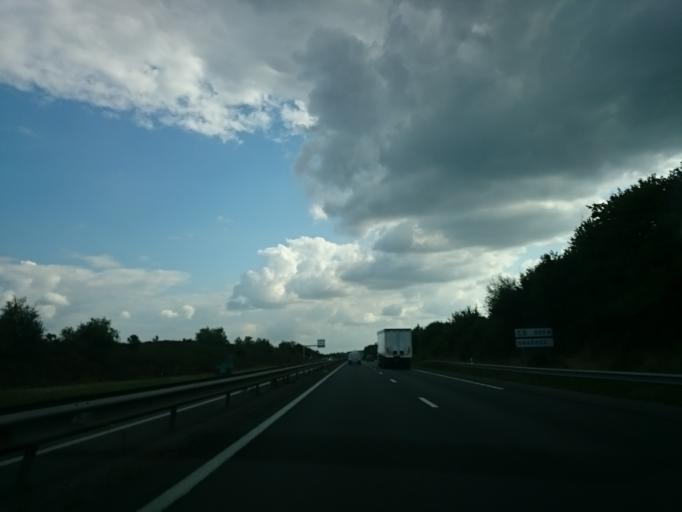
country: FR
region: Brittany
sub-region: Departement d'Ille-et-Vilaine
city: Chartres-de-Bretagne
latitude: 48.0186
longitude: -1.6910
